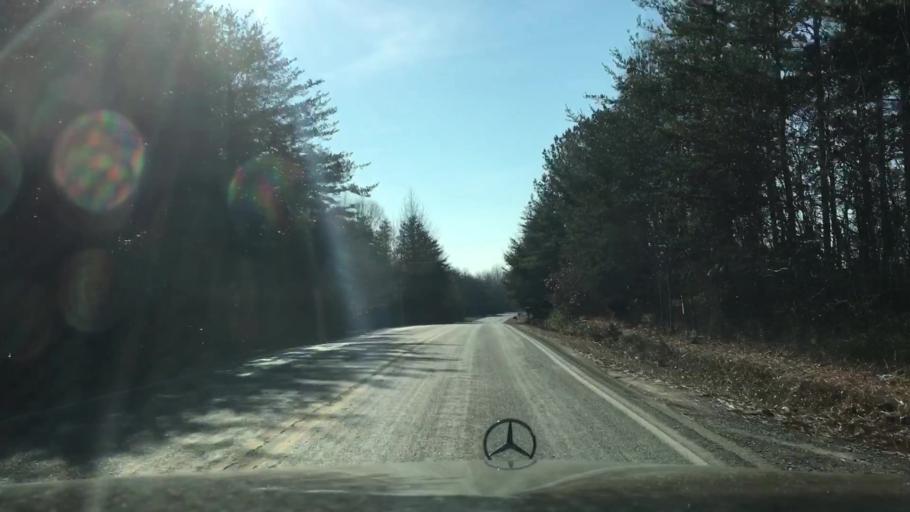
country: US
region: Virginia
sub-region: Pittsylvania County
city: Motley
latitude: 37.1800
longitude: -79.4101
